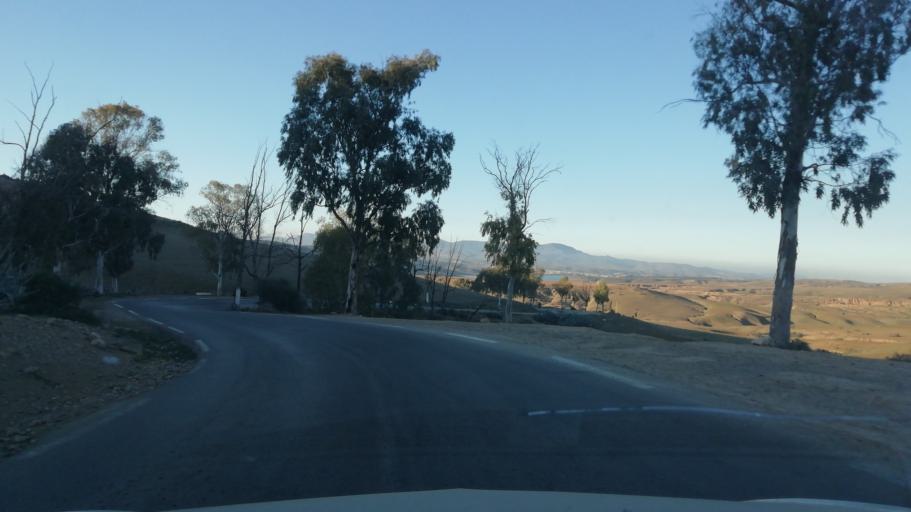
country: DZ
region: Tlemcen
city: Nedroma
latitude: 34.8254
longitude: -1.6387
